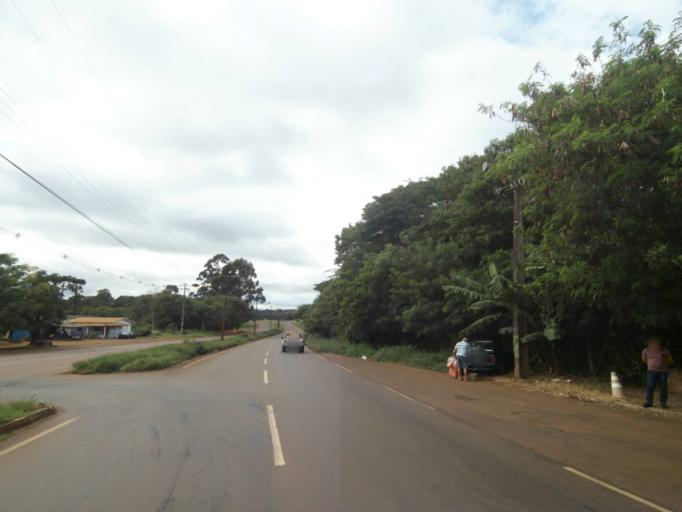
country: BR
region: Parana
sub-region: Campo Mourao
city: Campo Mourao
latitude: -24.0537
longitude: -52.3829
